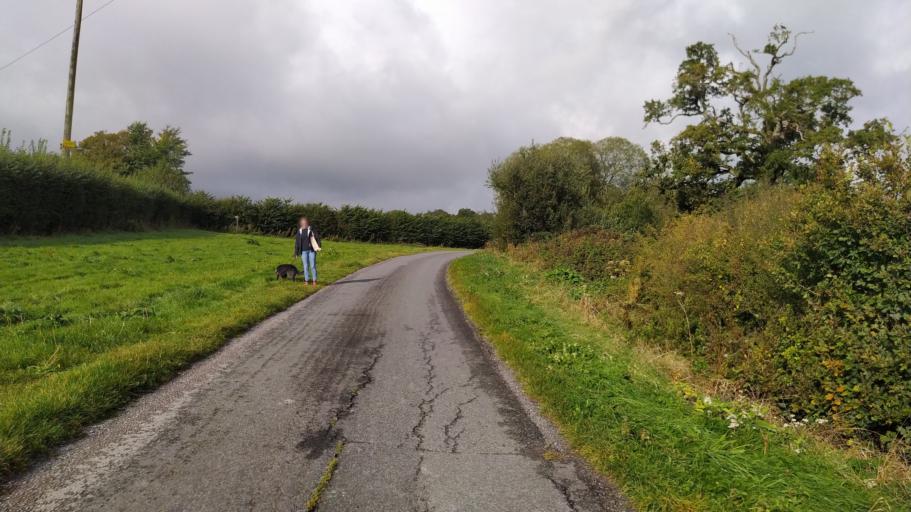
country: GB
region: England
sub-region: Dorset
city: Shaftesbury
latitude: 51.0396
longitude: -2.1502
